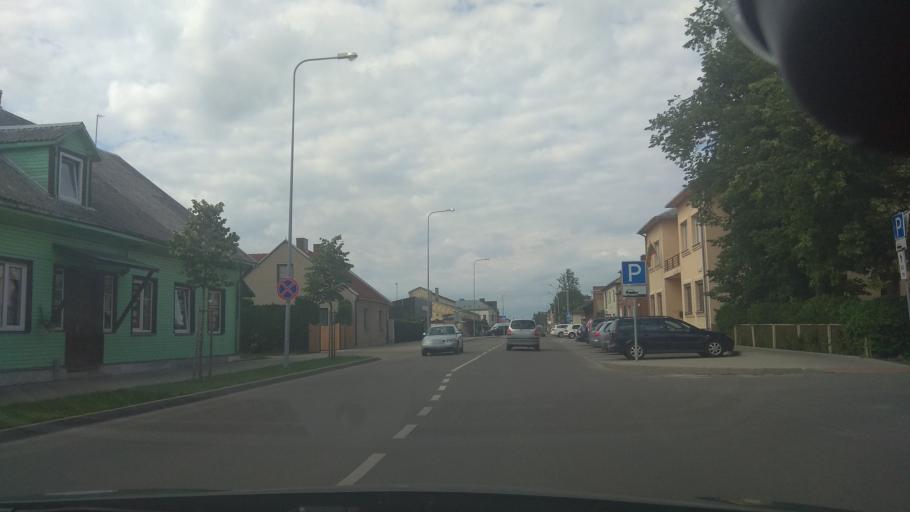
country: LT
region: Marijampoles apskritis
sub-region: Marijampole Municipality
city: Marijampole
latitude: 54.5527
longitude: 23.3536
